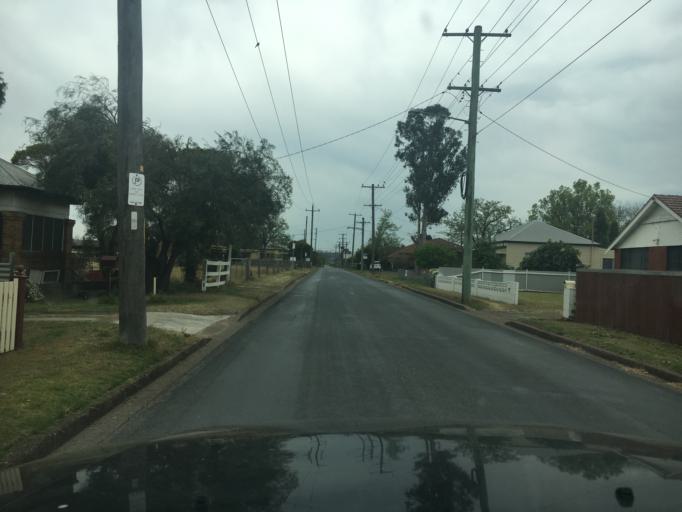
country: AU
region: New South Wales
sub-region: Maitland Municipality
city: Maitland
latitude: -32.7482
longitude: 151.5590
